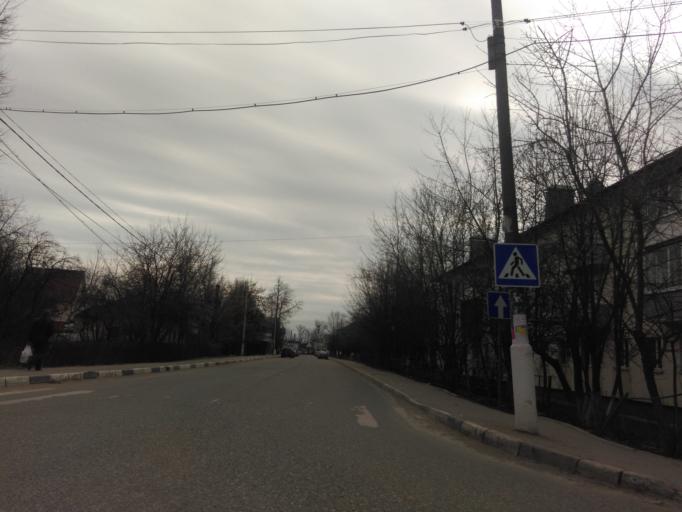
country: RU
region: Moskovskaya
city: Tuchkovo
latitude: 55.6009
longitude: 36.4679
